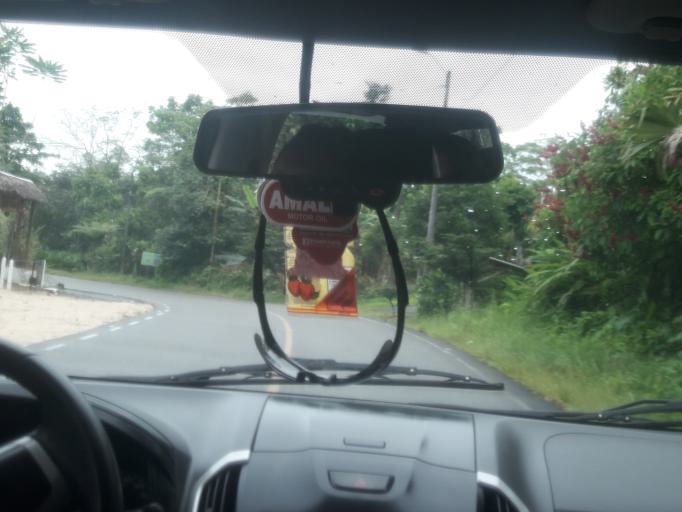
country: EC
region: Napo
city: Tena
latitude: -1.0358
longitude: -77.6904
